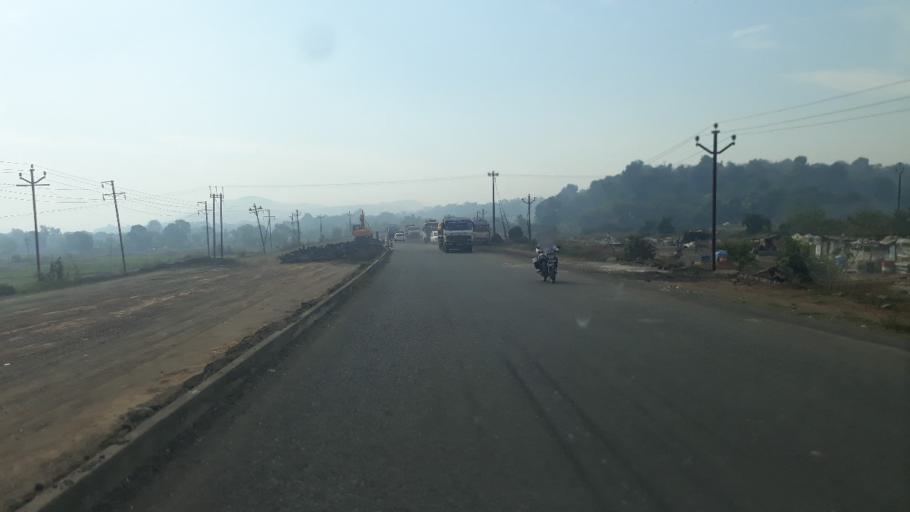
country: IN
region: Maharashtra
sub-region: Raigarh
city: Pen
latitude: 18.7988
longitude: 73.0923
